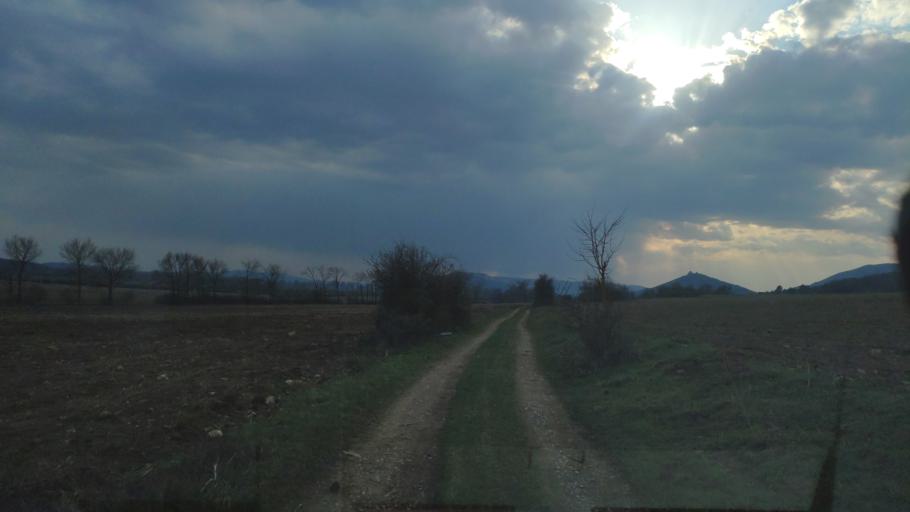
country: SK
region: Kosicky
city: Moldava nad Bodvou
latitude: 48.6183
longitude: 20.9302
